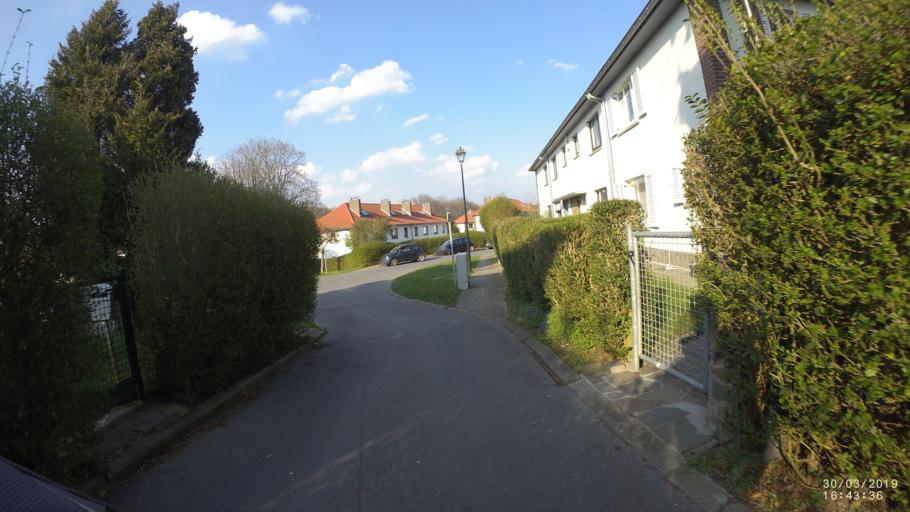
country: BE
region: Flanders
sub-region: Provincie Vlaams-Brabant
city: Kraainem
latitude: 50.8400
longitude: 4.4436
